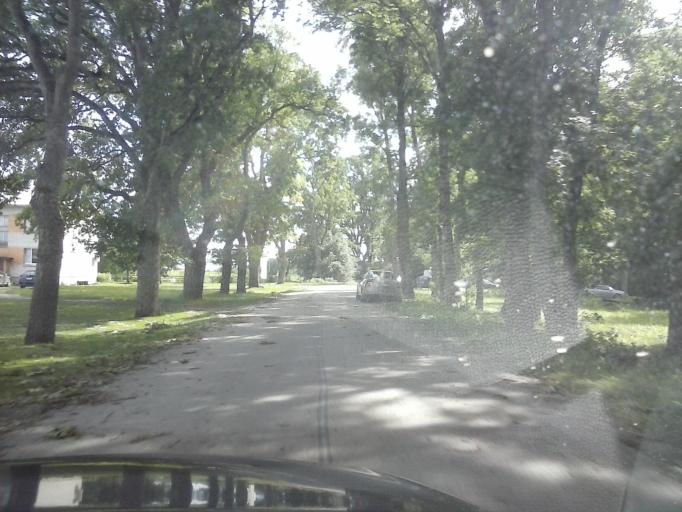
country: EE
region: Laeaene-Virumaa
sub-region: Vaeike-Maarja vald
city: Vaike-Maarja
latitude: 59.0784
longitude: 26.1964
